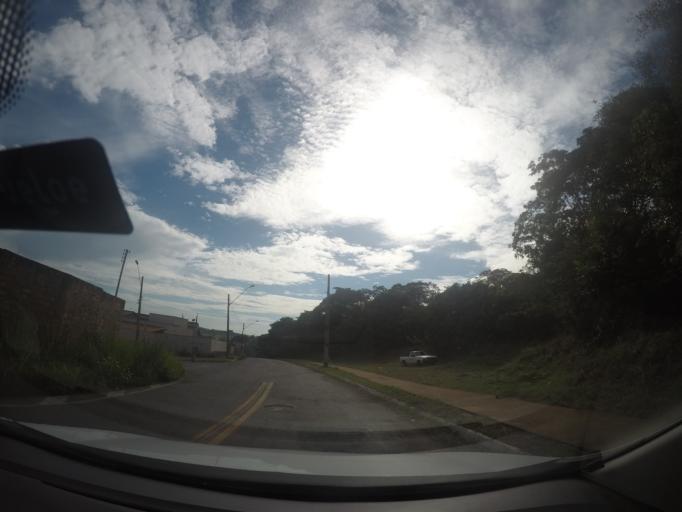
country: BR
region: Goias
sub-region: Goiania
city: Goiania
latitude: -16.6868
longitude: -49.2028
